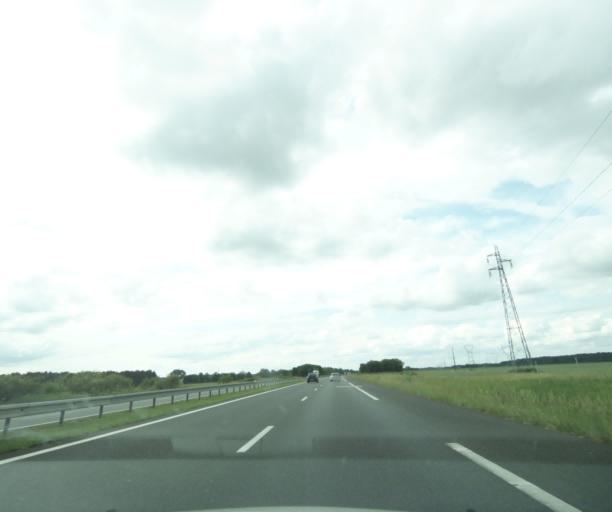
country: FR
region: Centre
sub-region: Departement du Cher
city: Marmagne
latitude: 47.0693
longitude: 2.2852
